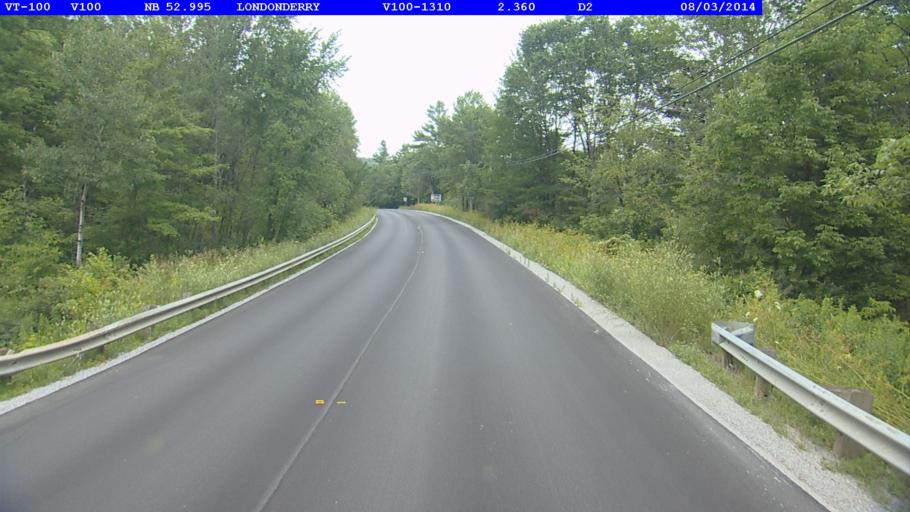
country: US
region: Vermont
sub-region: Windsor County
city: Chester
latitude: 43.1842
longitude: -72.8144
